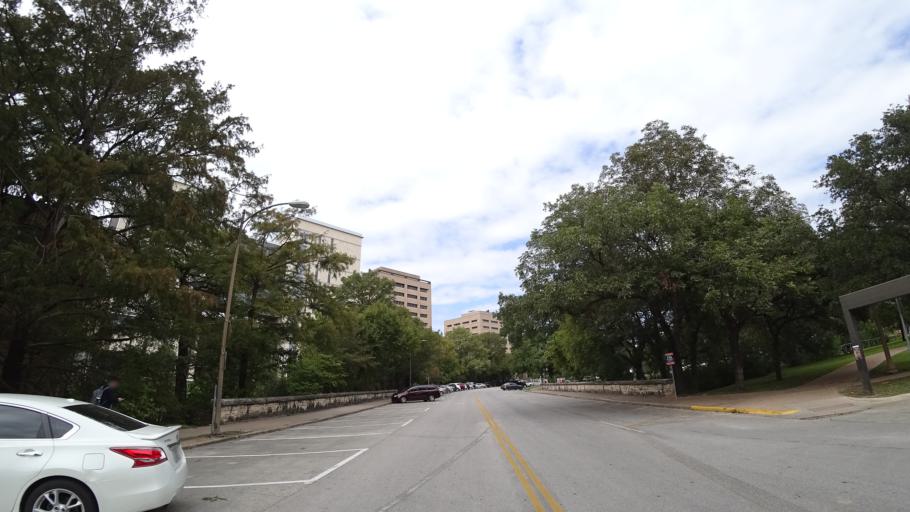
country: US
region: Texas
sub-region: Travis County
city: Austin
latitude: 30.2880
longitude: -97.7339
